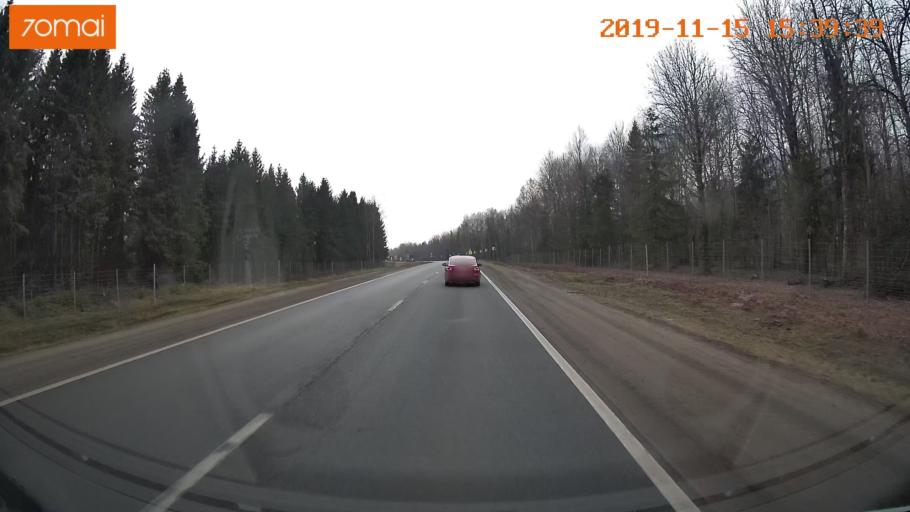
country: RU
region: Jaroslavl
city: Danilov
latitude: 58.0193
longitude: 40.0655
